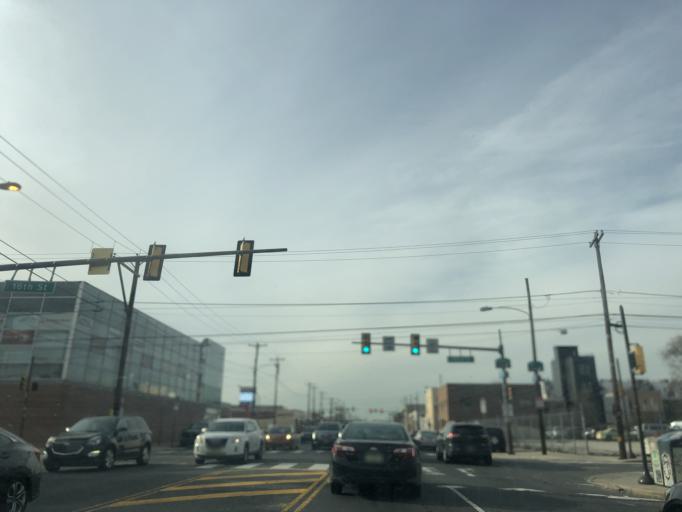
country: US
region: Pennsylvania
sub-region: Philadelphia County
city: Philadelphia
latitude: 39.9383
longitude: -75.1697
